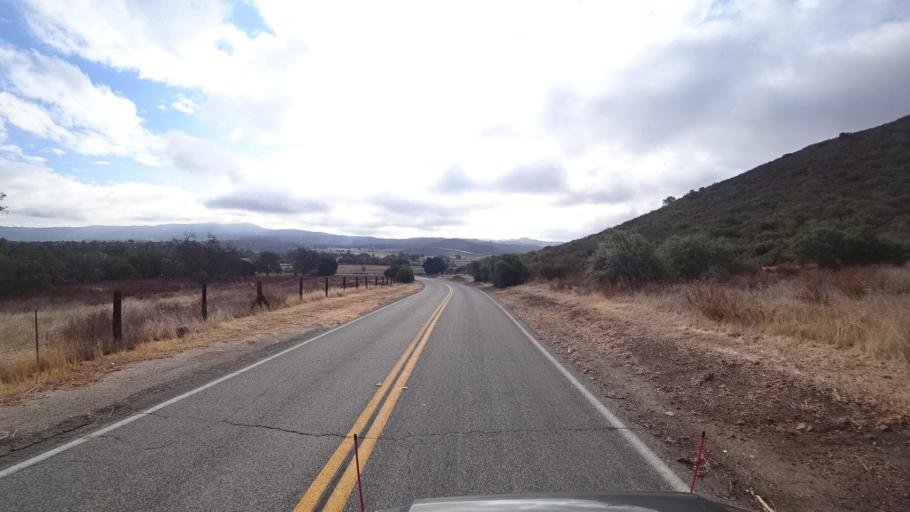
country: MX
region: Baja California
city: Tecate
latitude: 32.6229
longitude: -116.6213
